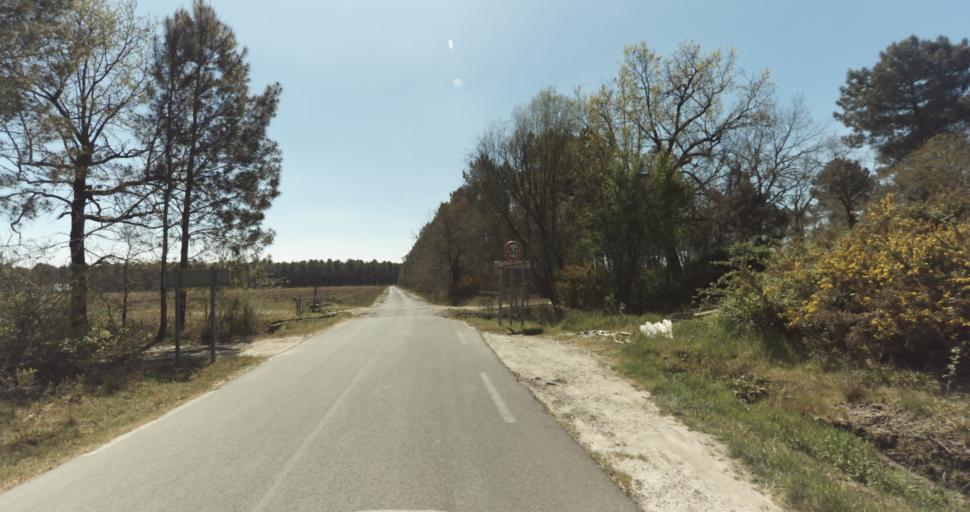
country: FR
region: Aquitaine
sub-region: Departement de la Gironde
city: Martignas-sur-Jalle
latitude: 44.8037
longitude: -0.7527
